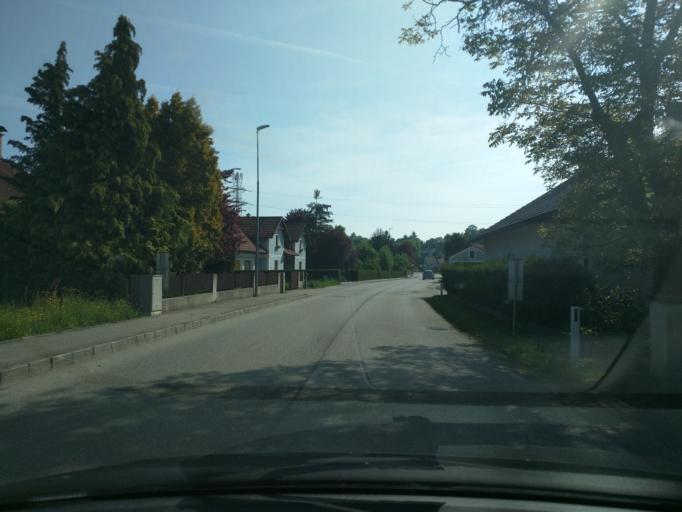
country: AT
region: Lower Austria
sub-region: Politischer Bezirk Amstetten
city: Allhartsberg
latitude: 48.0426
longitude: 14.7899
